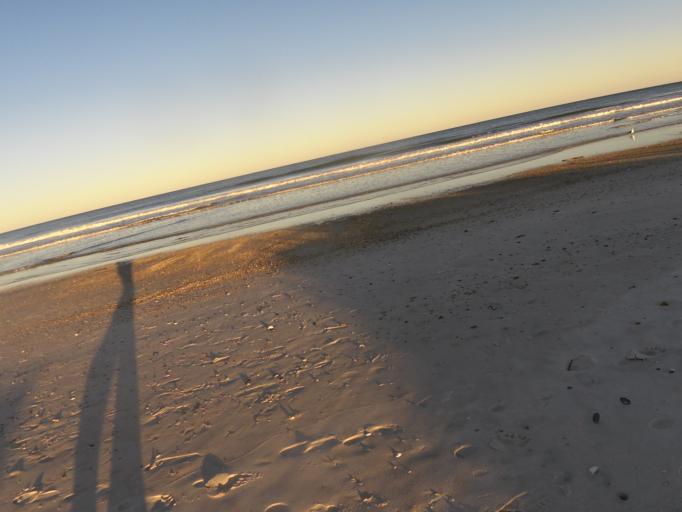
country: US
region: Florida
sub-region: Duval County
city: Atlantic Beach
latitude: 30.4639
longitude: -81.4118
